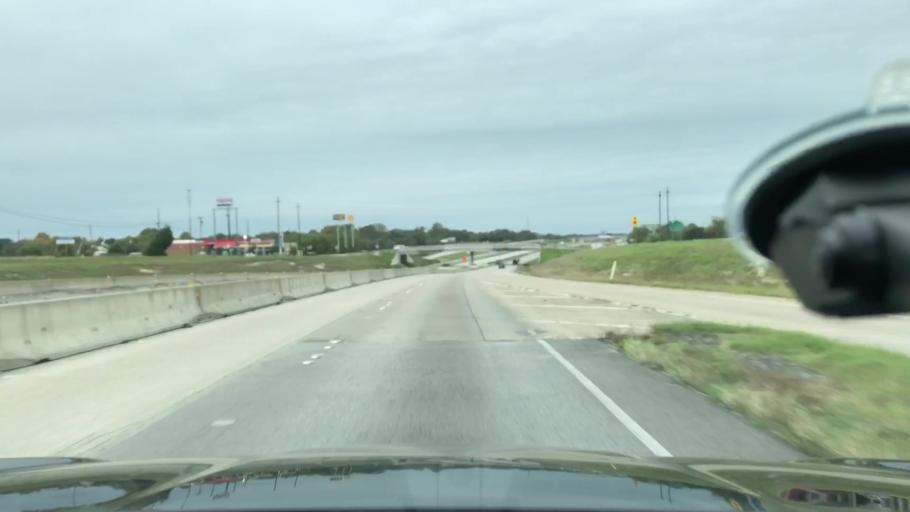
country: US
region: Texas
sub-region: Ellis County
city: Waxahachie
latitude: 32.3720
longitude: -96.8618
